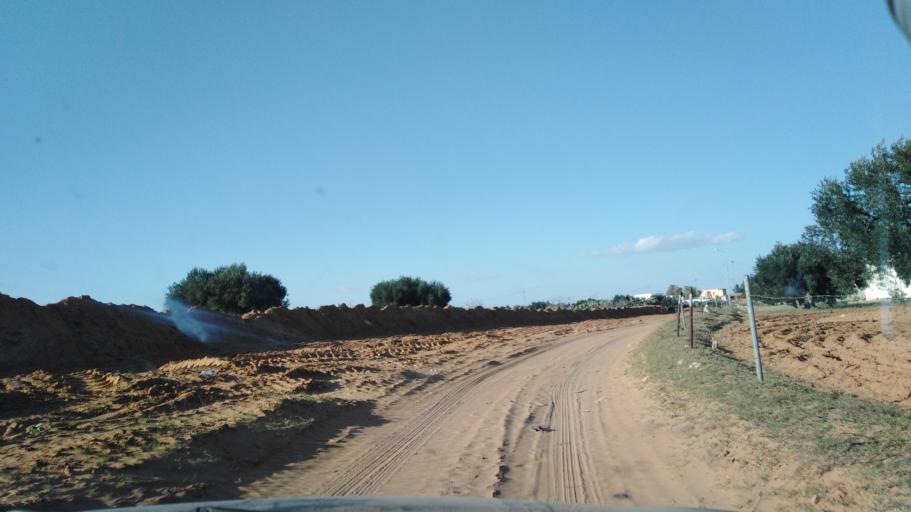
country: TN
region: Al Mahdiyah
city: Shurban
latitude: 34.9561
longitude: 10.3633
